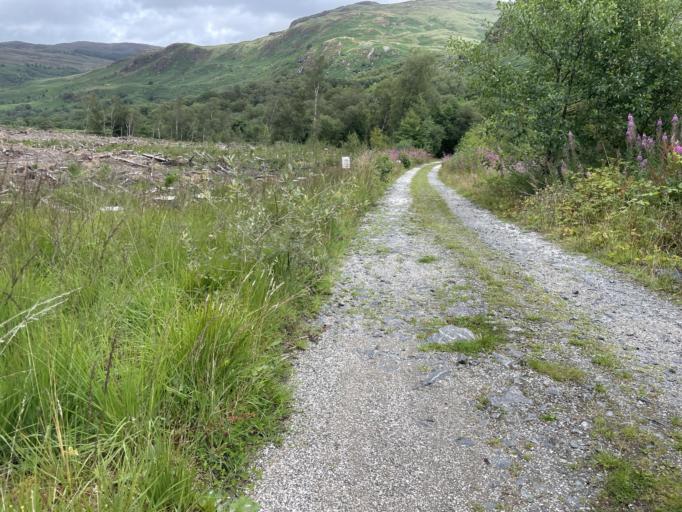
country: GB
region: Scotland
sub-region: Dumfries and Galloway
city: Newton Stewart
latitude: 55.0879
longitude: -4.4580
